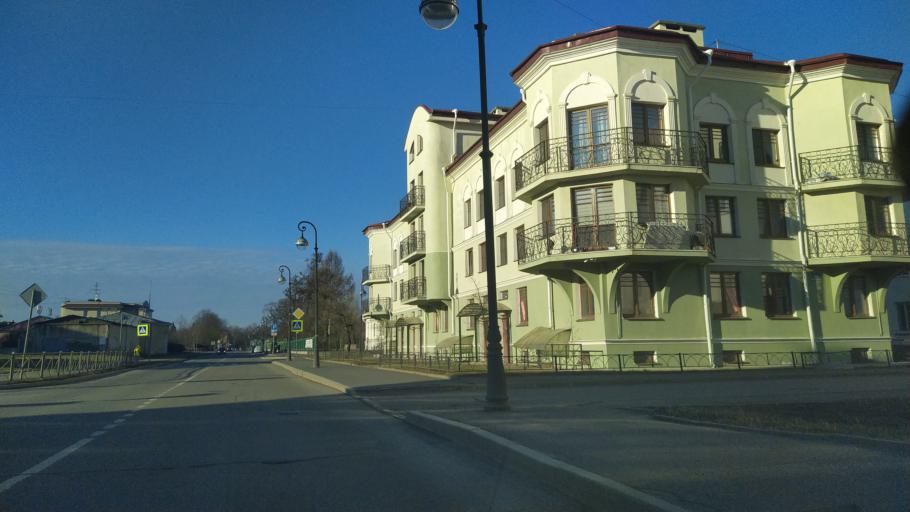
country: RU
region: St.-Petersburg
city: Pushkin
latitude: 59.7033
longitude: 30.3930
